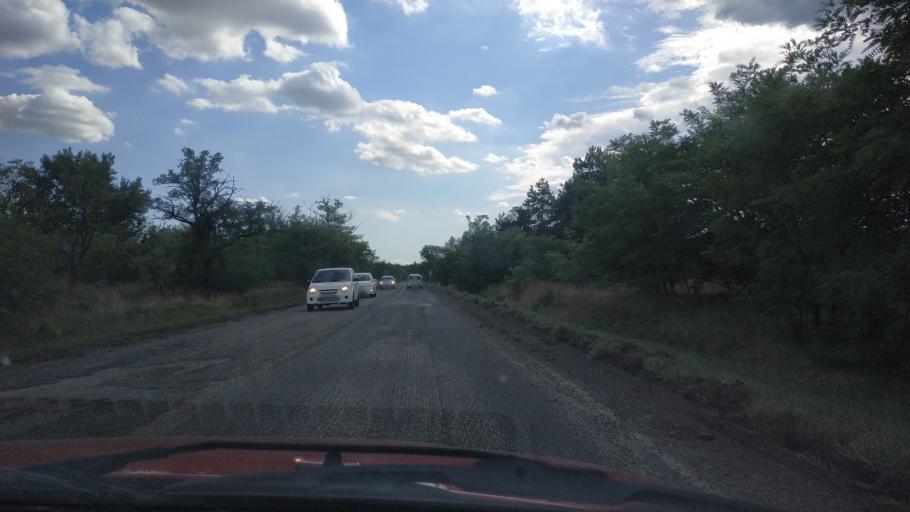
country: HU
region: Fejer
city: Zamoly
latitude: 47.3535
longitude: 18.4230
